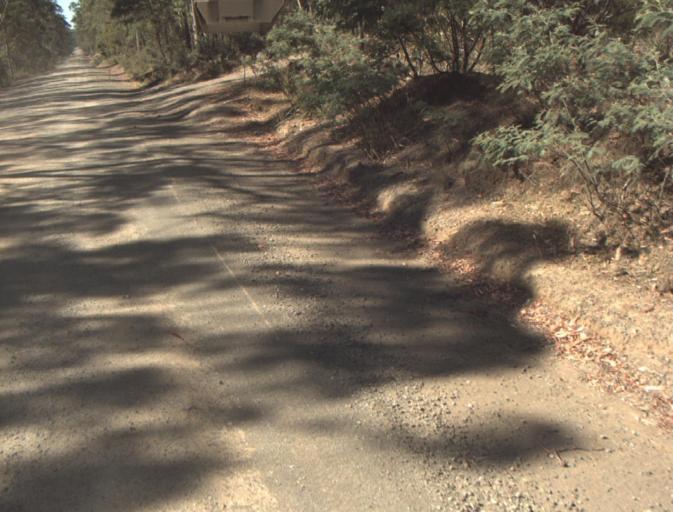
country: AU
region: Tasmania
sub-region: Launceston
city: Mayfield
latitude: -41.3411
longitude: 147.2107
